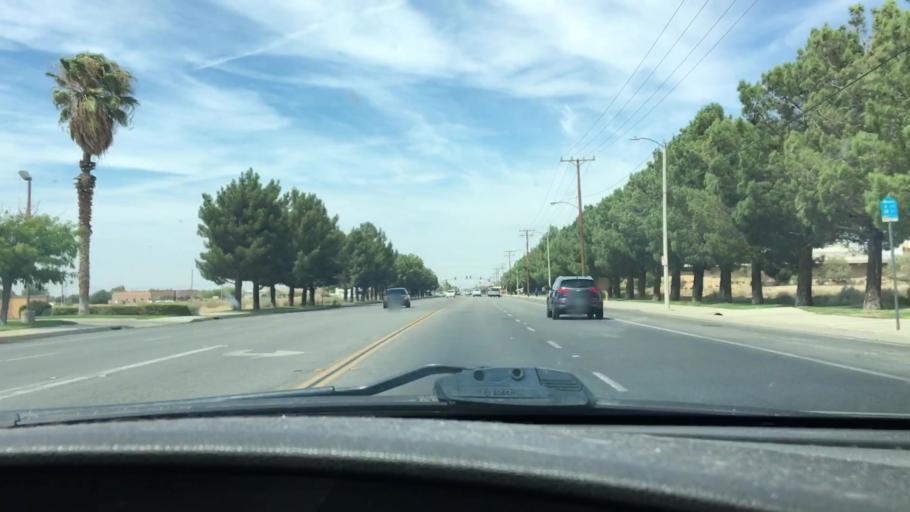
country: US
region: California
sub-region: Los Angeles County
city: Lancaster
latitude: 34.6716
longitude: -118.1301
